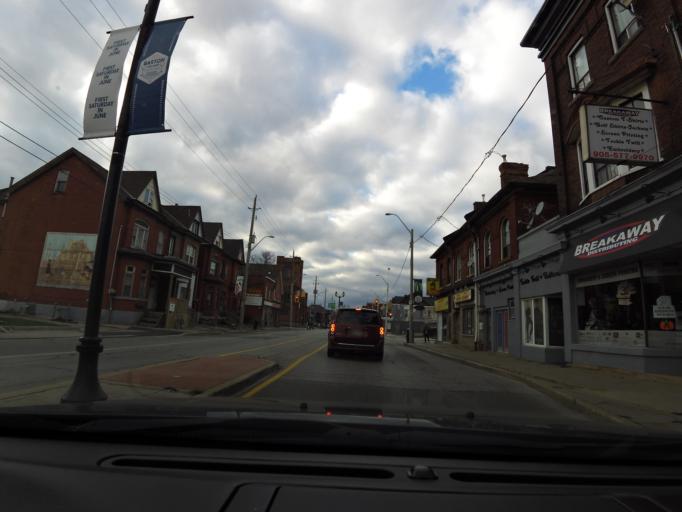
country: CA
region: Ontario
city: Hamilton
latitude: 43.2597
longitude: -79.8481
